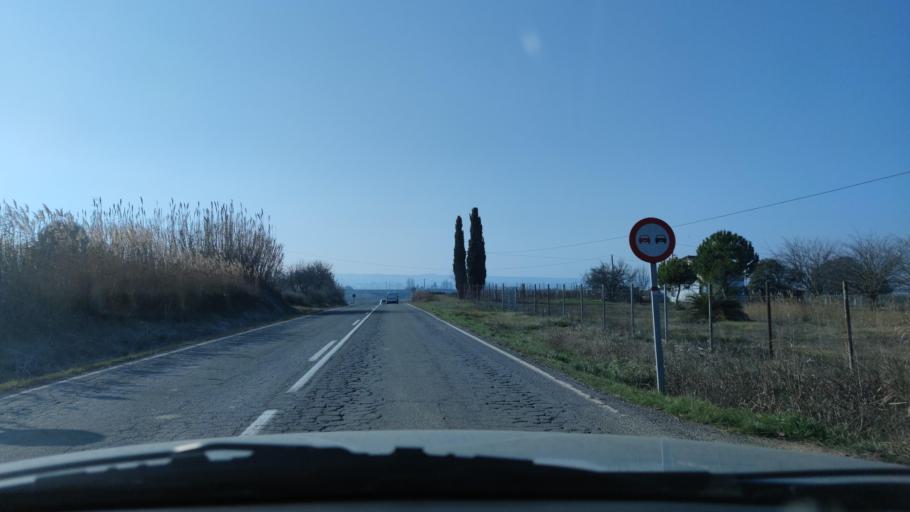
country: ES
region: Catalonia
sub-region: Provincia de Lleida
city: Juneda
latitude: 41.5589
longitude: 0.7435
